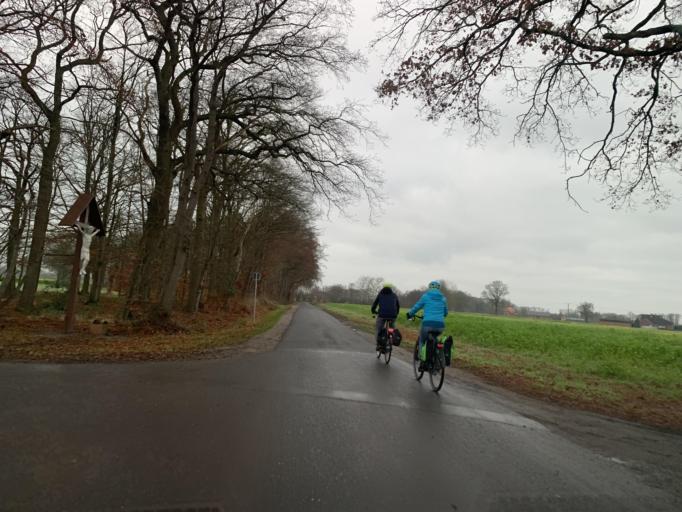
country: DE
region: North Rhine-Westphalia
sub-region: Regierungsbezirk Munster
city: Greven
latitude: 52.0699
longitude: 7.5466
